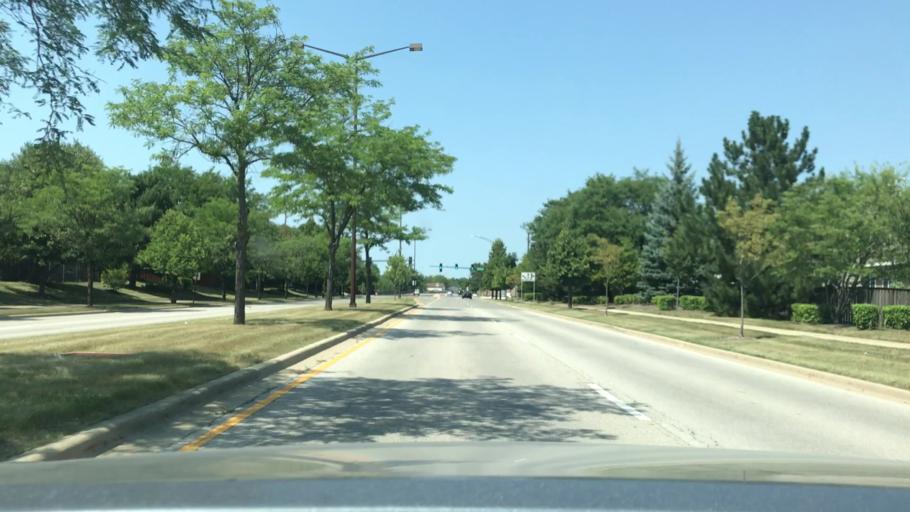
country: US
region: Illinois
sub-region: Kane County
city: Aurora
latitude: 41.7230
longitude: -88.2547
